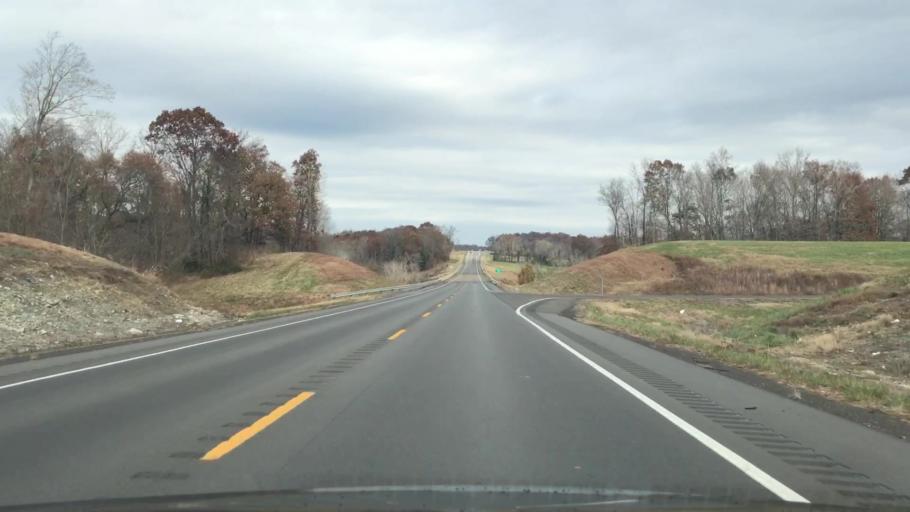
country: US
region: Kentucky
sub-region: Monroe County
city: Tompkinsville
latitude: 36.8020
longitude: -85.6876
